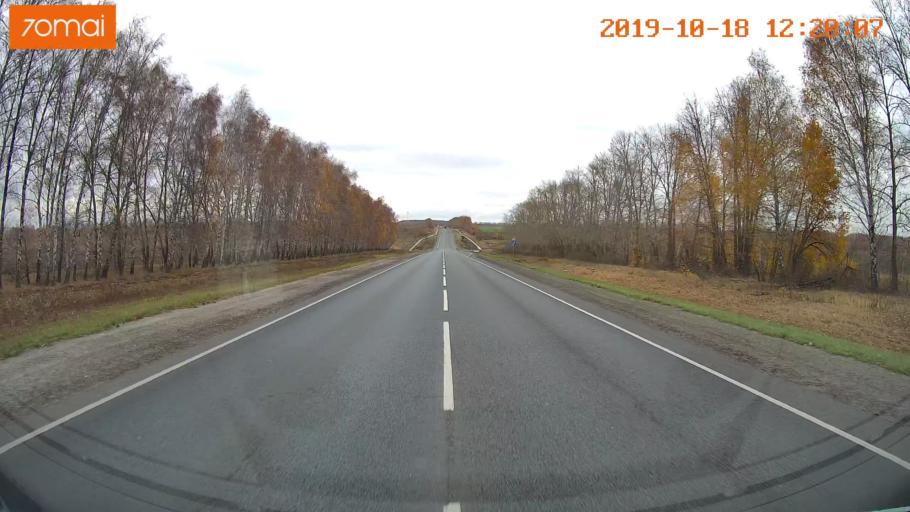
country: RU
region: Rjazan
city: Bagramovo
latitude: 54.4925
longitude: 39.4760
